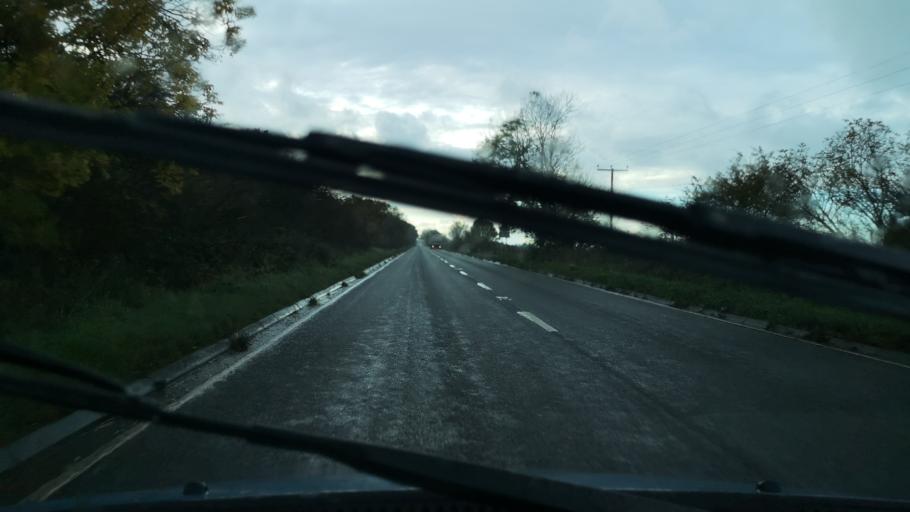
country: GB
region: England
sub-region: North Lincolnshire
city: Crowle
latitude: 53.5852
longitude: -0.8417
